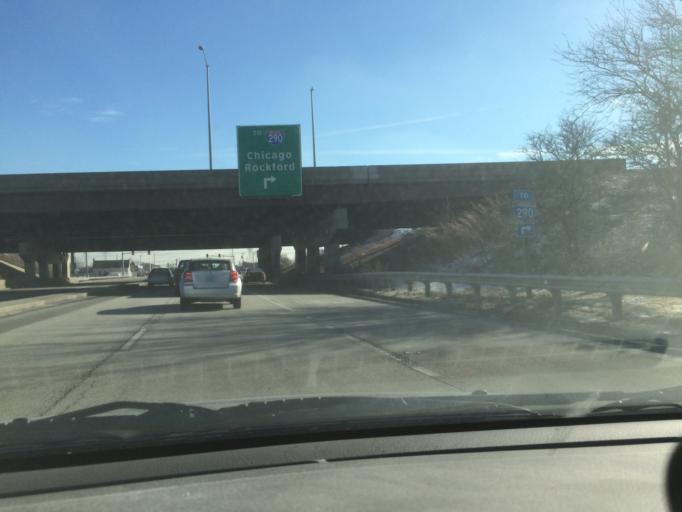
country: US
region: Illinois
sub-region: DuPage County
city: Itasca
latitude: 41.9518
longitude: -88.0356
